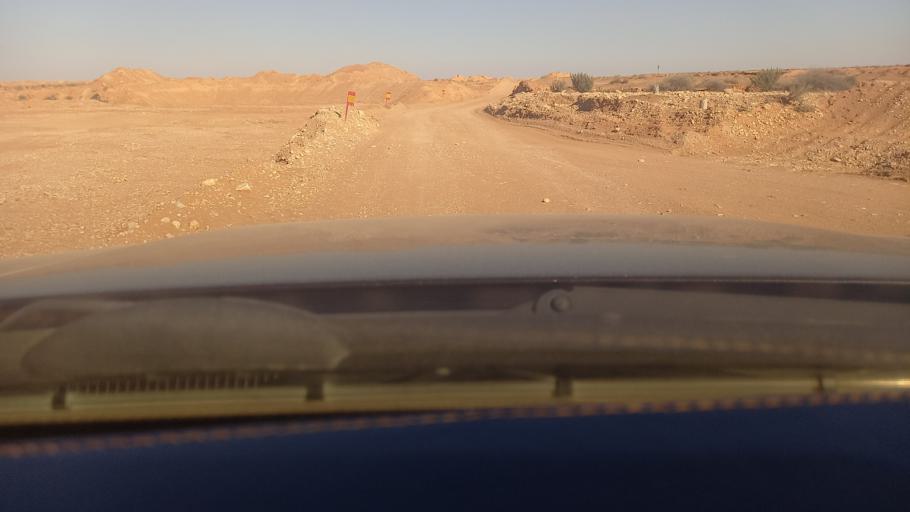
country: TN
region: Madanin
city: Medenine
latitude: 33.1474
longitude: 10.5072
